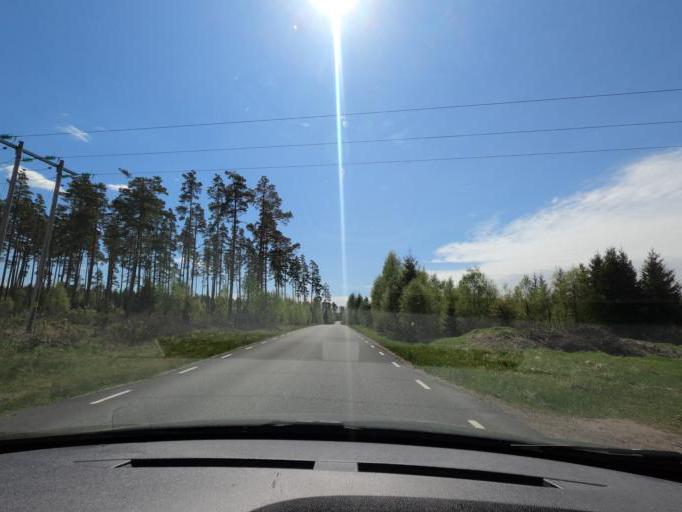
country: SE
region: Joenkoeping
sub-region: Varnamo Kommun
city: Bredaryd
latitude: 57.1608
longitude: 13.7353
